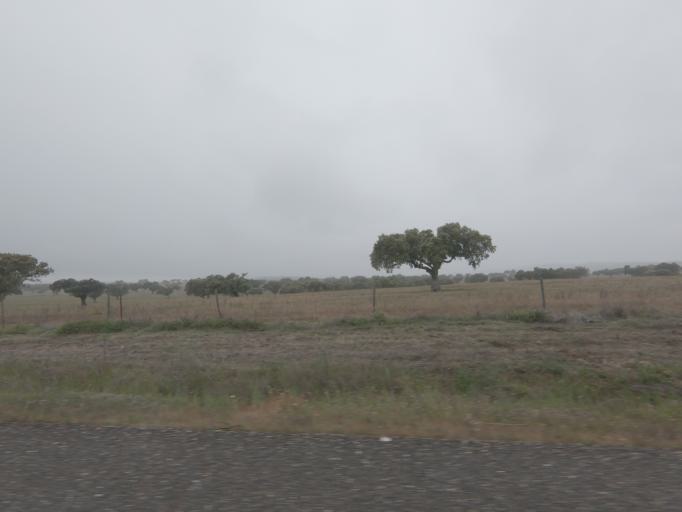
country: ES
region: Extremadura
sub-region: Provincia de Badajoz
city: La Roca de la Sierra
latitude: 39.1042
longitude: -6.7104
